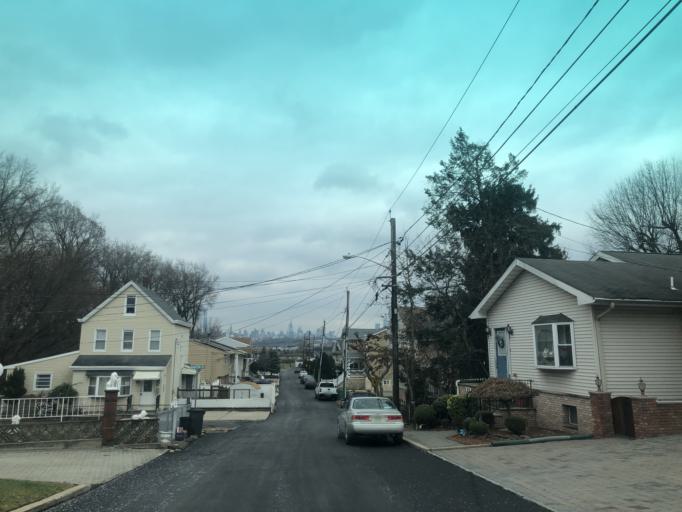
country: US
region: New Jersey
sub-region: Hudson County
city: Secaucus
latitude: 40.7992
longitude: -74.0522
